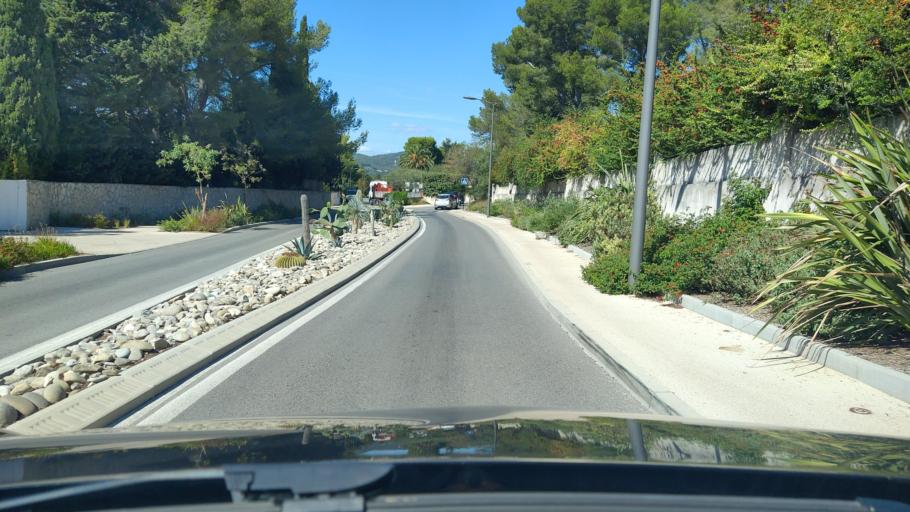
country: FR
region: Provence-Alpes-Cote d'Azur
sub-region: Departement du Var
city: Sanary-sur-Mer
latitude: 43.1349
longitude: 5.7885
